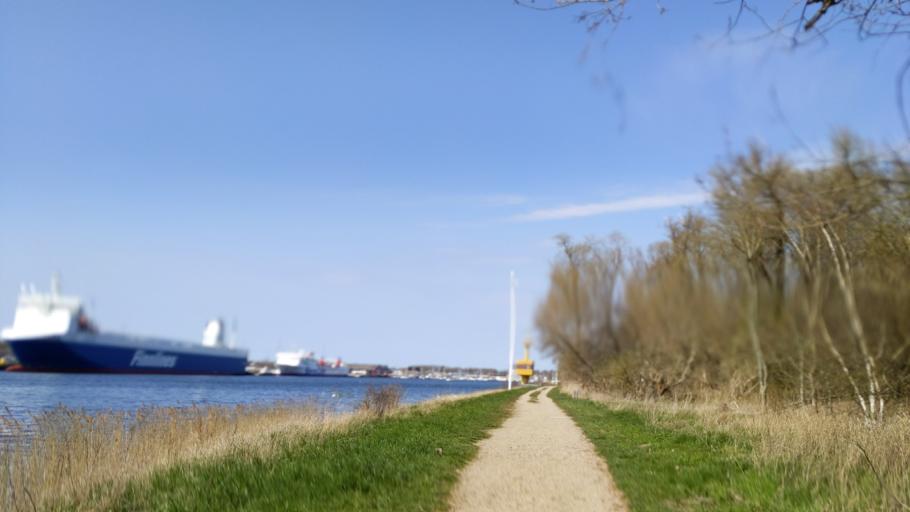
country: DE
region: Schleswig-Holstein
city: Travemuende
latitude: 53.9441
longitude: 10.8642
